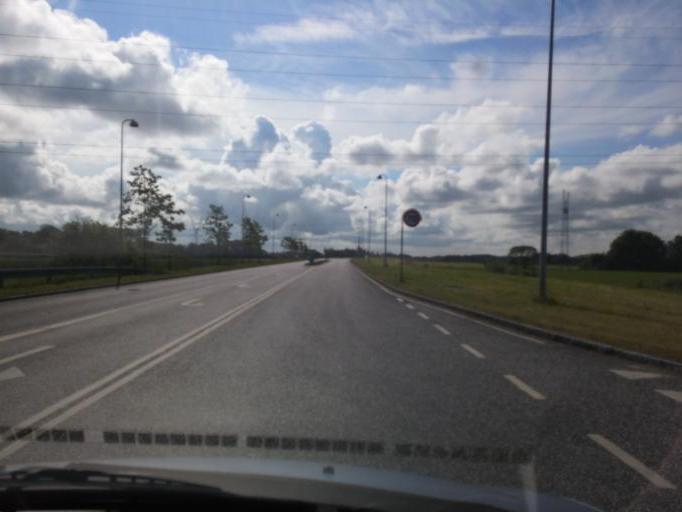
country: DK
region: South Denmark
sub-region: Odense Kommune
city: Neder Holluf
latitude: 55.3710
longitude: 10.5058
